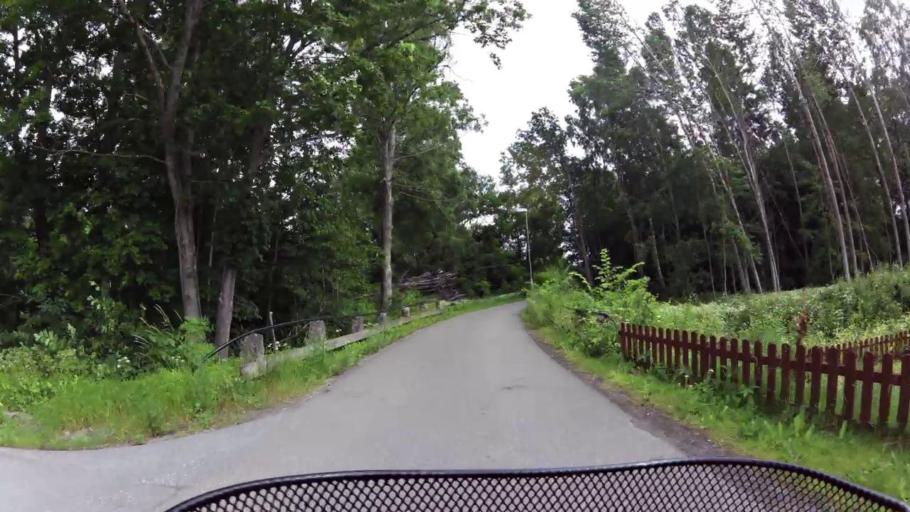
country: SE
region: OEstergoetland
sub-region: Linkopings Kommun
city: Malmslatt
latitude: 58.4128
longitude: 15.5264
